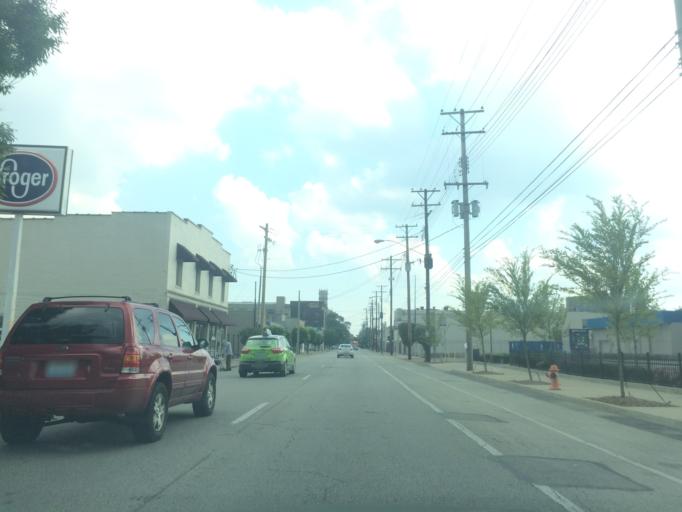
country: US
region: Kentucky
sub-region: Jefferson County
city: Louisville
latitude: 38.2409
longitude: -85.7576
